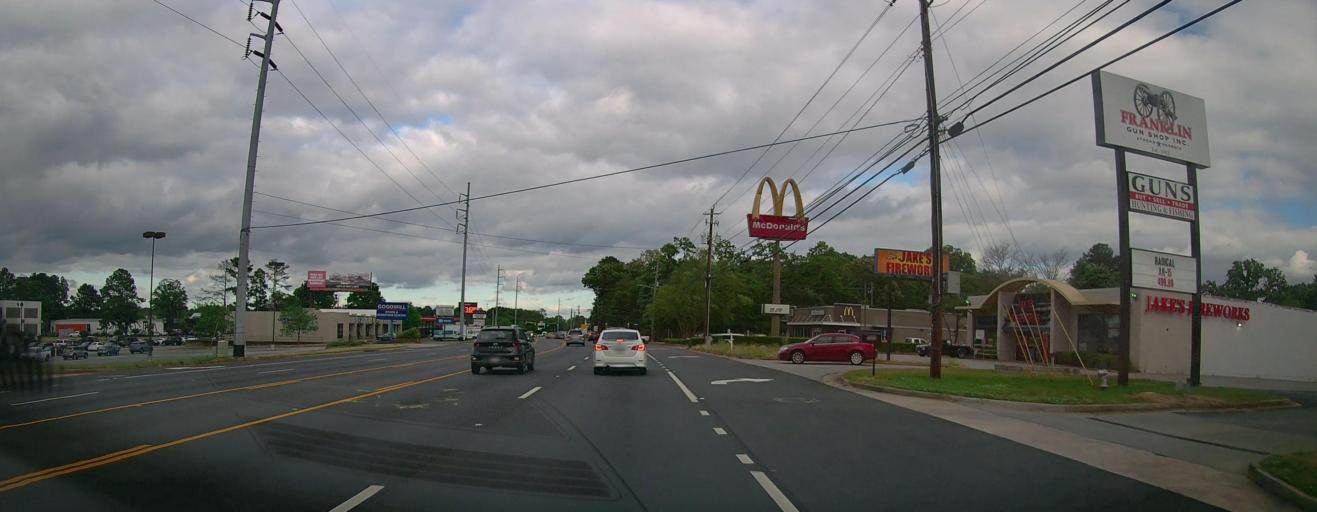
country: US
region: Georgia
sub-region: Oconee County
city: Bogart
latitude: 33.9405
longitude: -83.4731
